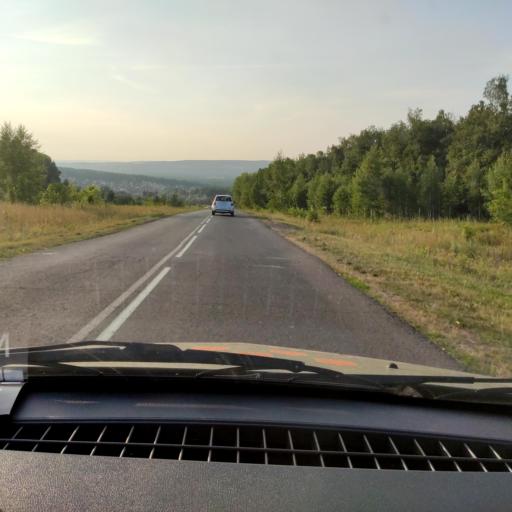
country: RU
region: Bashkortostan
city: Avdon
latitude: 54.5725
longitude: 55.6748
